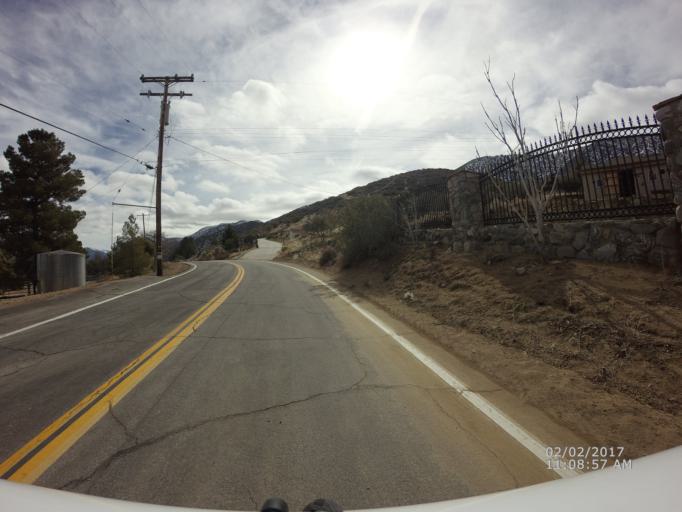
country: US
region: California
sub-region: Los Angeles County
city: Littlerock
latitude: 34.4310
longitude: -117.9228
